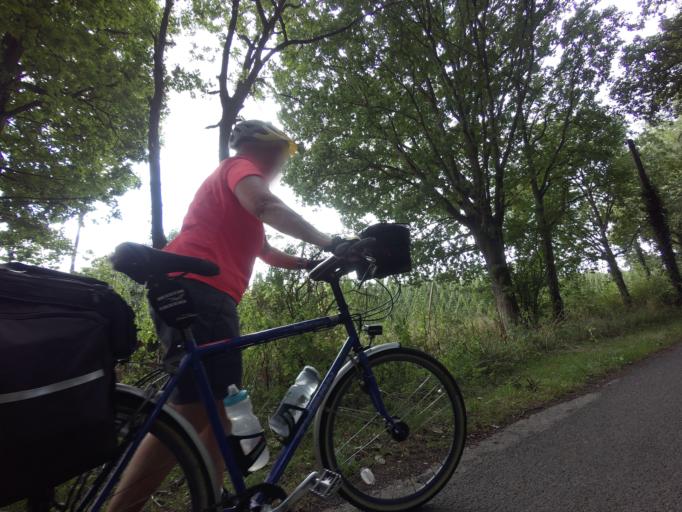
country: GB
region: England
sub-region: Kent
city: Marden
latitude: 51.1494
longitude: 0.5006
